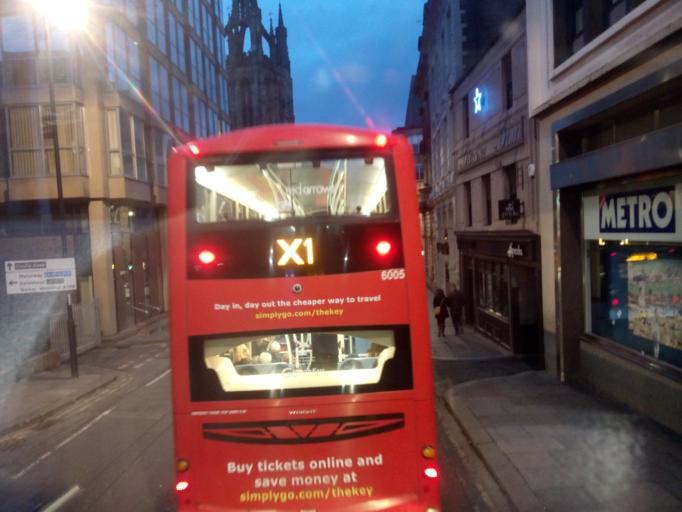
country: GB
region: England
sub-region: Newcastle upon Tyne
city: Newcastle upon Tyne
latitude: 54.9709
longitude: -1.6124
